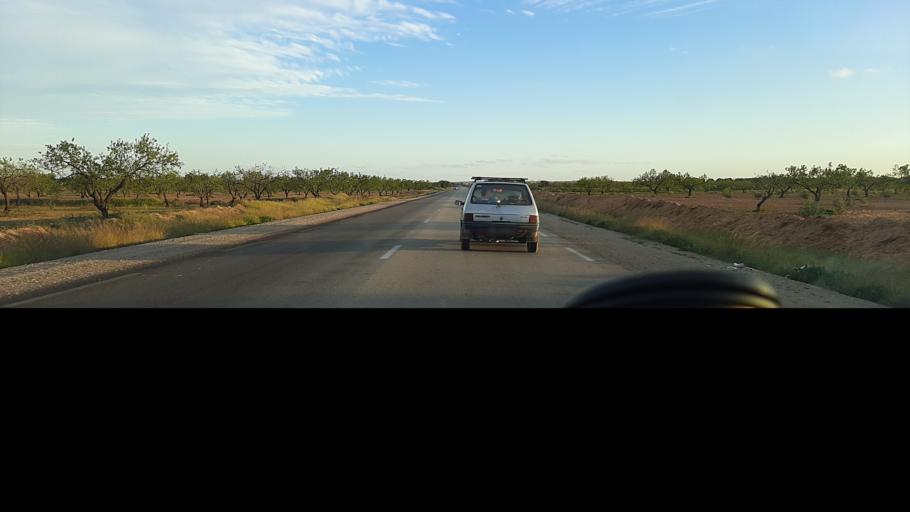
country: TN
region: Safaqis
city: Sfax
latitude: 34.9169
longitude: 10.6297
